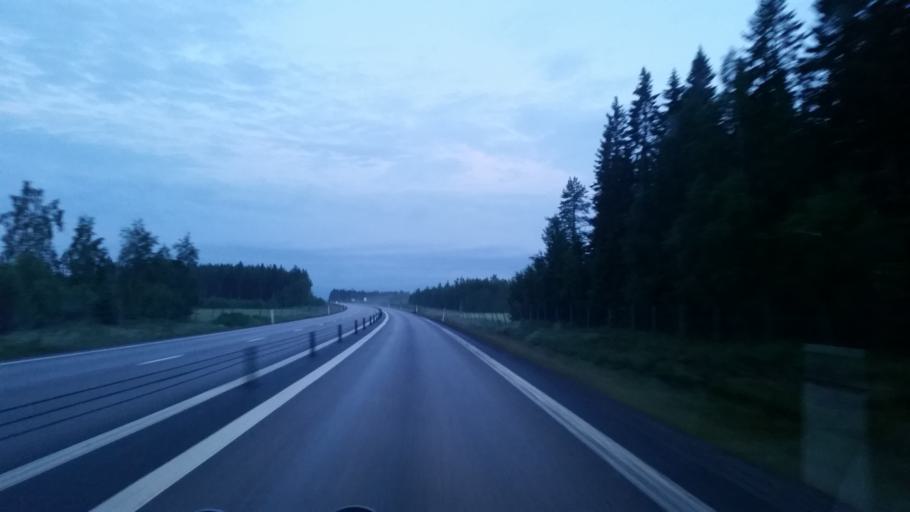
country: SE
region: Vaesterbotten
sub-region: Robertsfors Kommun
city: Robertsfors
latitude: 64.1231
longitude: 20.8834
